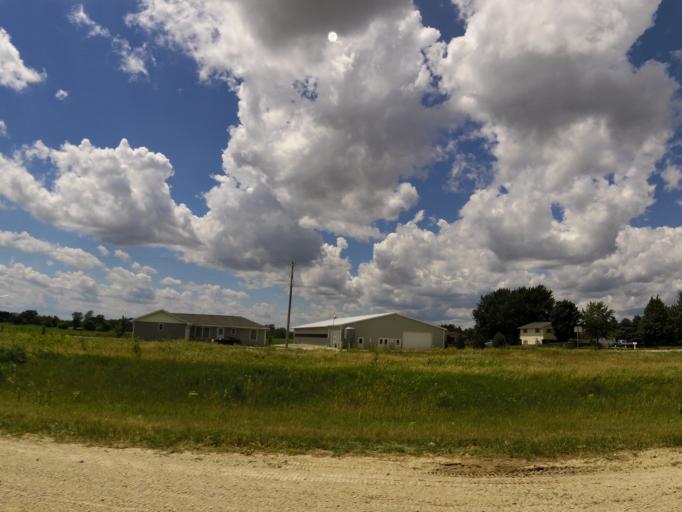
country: US
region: Iowa
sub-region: Fayette County
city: Oelwein
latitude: 42.5875
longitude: -91.9042
